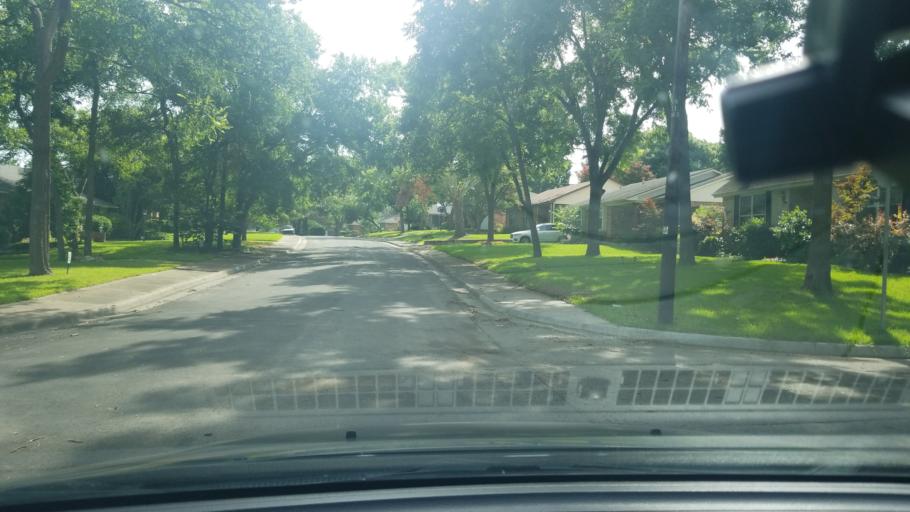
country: US
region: Texas
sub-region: Dallas County
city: Highland Park
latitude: 32.8077
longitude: -96.6992
